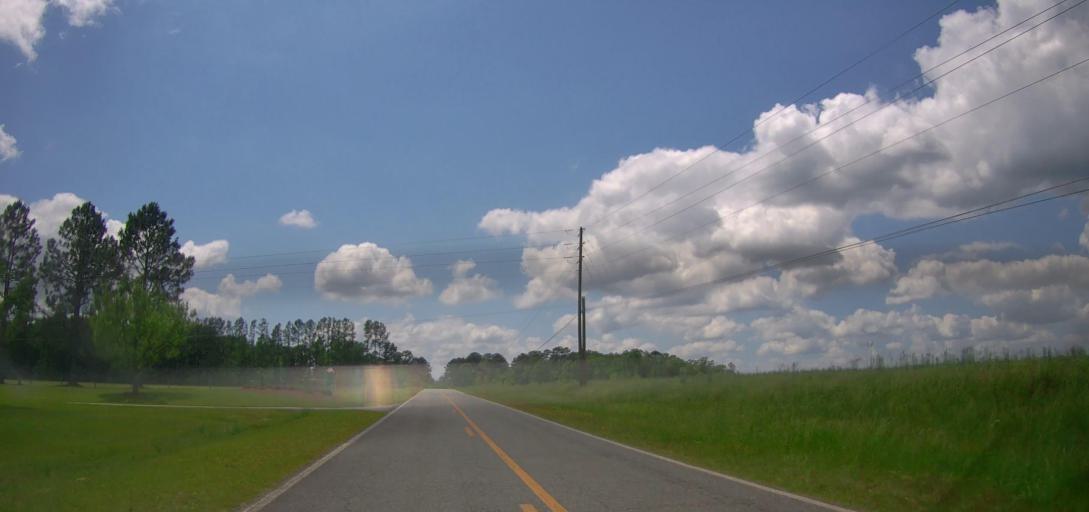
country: US
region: Georgia
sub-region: Laurens County
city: Dublin
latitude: 32.5927
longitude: -82.9350
